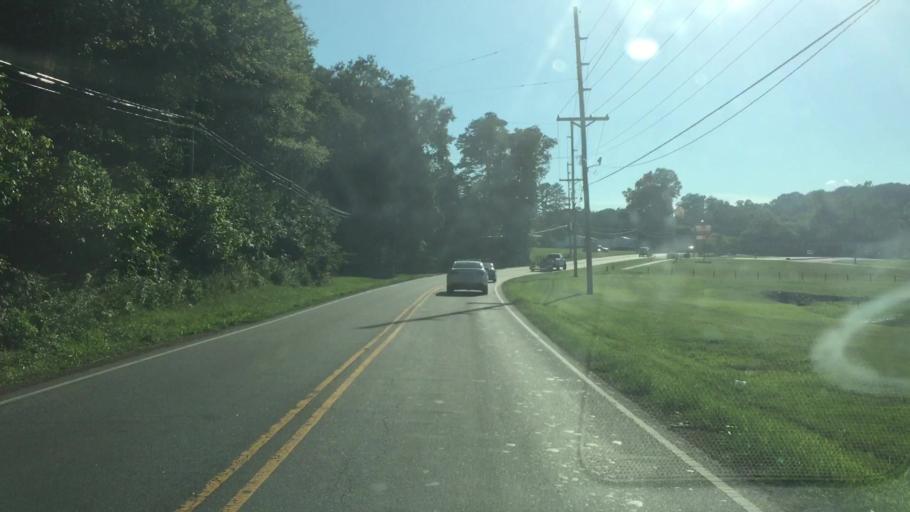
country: US
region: North Carolina
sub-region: Cabarrus County
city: Concord
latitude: 35.4120
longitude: -80.6226
